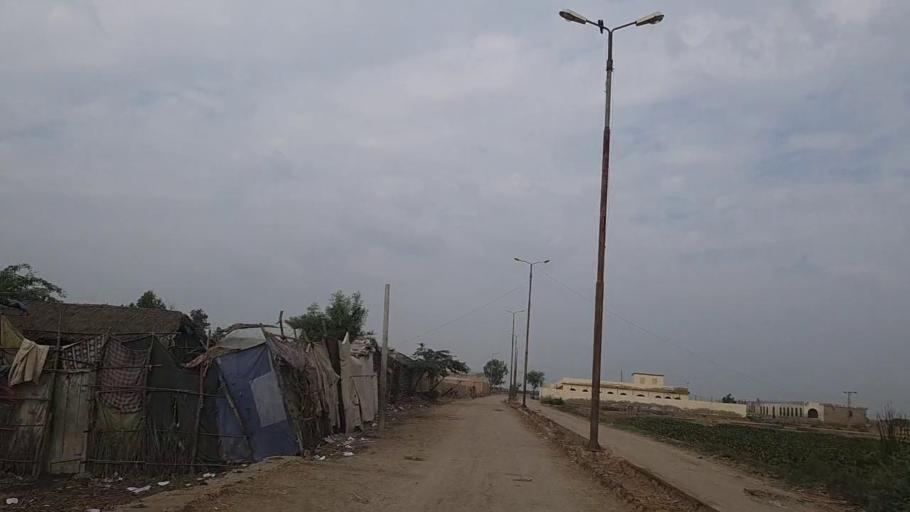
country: PK
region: Sindh
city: Daro Mehar
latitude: 24.6106
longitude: 68.0852
